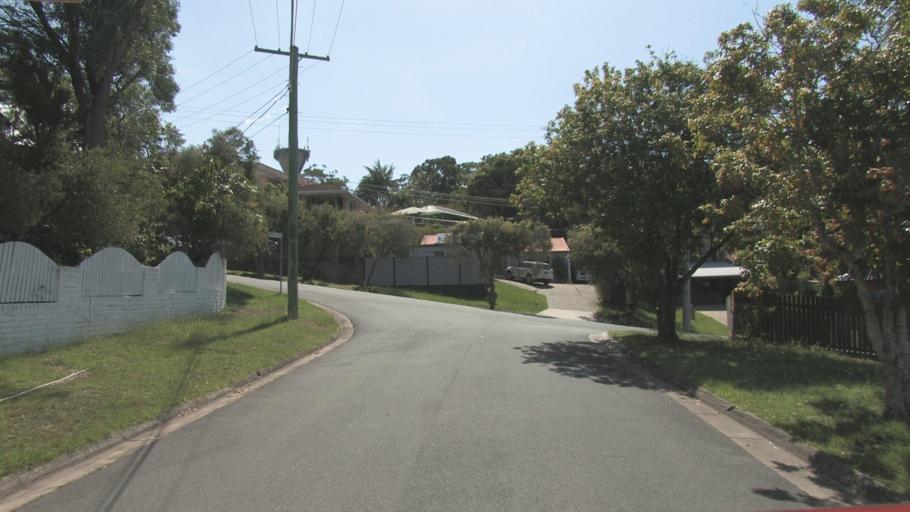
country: AU
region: Queensland
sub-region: Logan
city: Rochedale South
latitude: -27.6004
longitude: 153.1338
